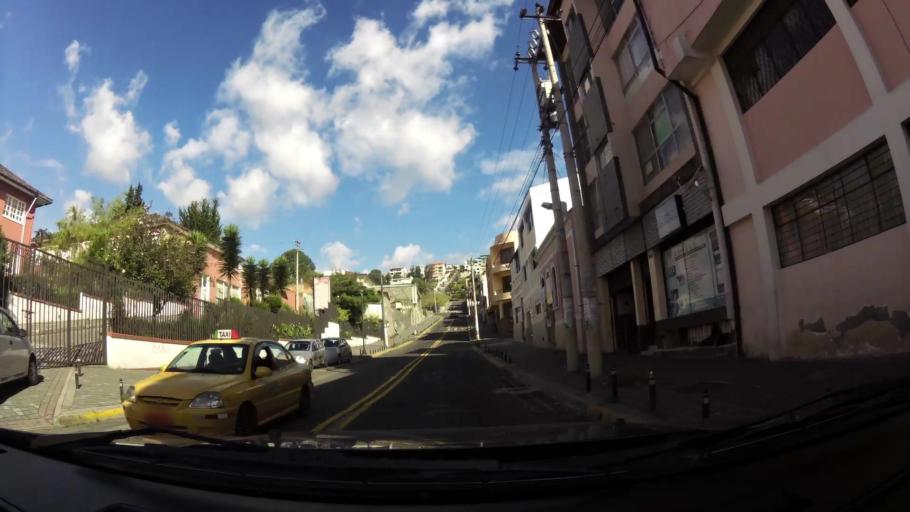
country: EC
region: Pichincha
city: Quito
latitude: -0.2154
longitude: -78.5002
